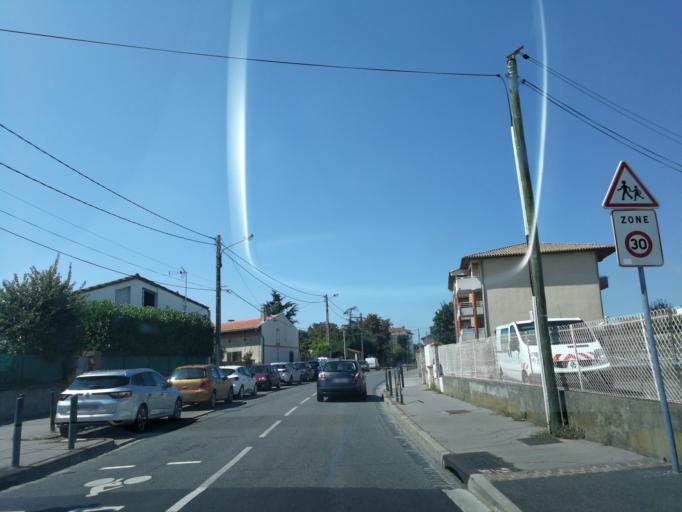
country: FR
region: Midi-Pyrenees
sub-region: Departement de la Haute-Garonne
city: L'Union
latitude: 43.6339
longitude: 1.4682
